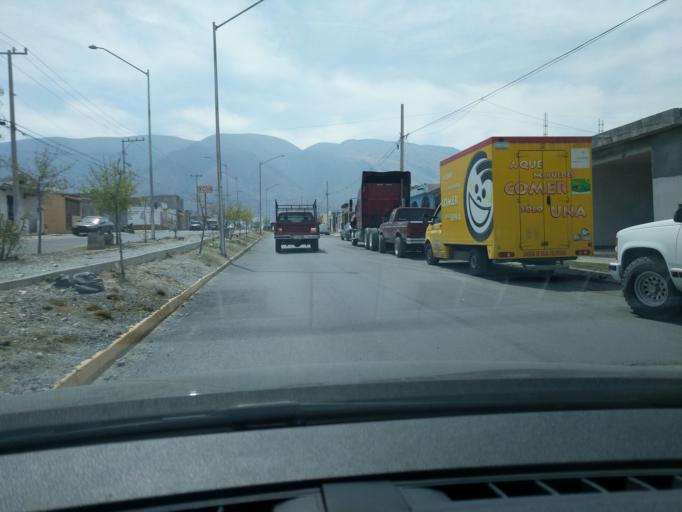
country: MX
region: Coahuila
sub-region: Arteaga
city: Arteaga
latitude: 25.4200
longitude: -100.9009
